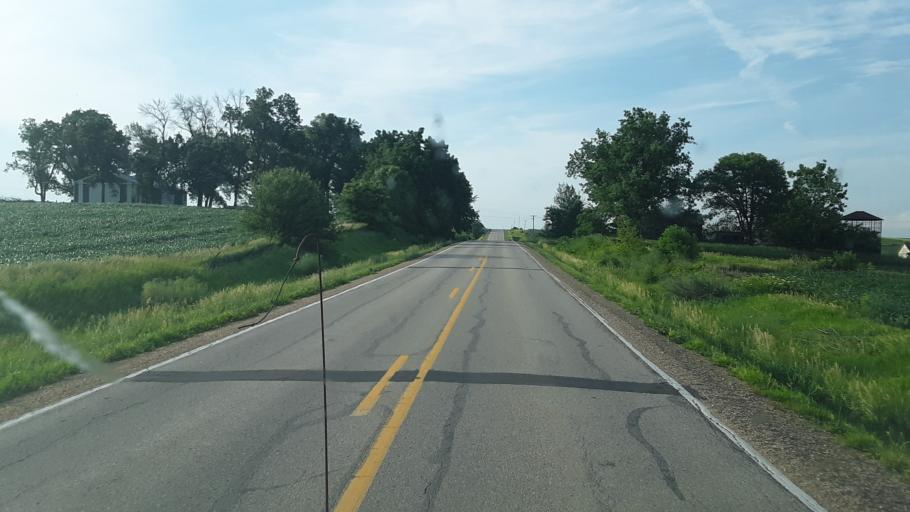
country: US
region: Iowa
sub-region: Tama County
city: Tama
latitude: 41.9519
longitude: -92.7077
